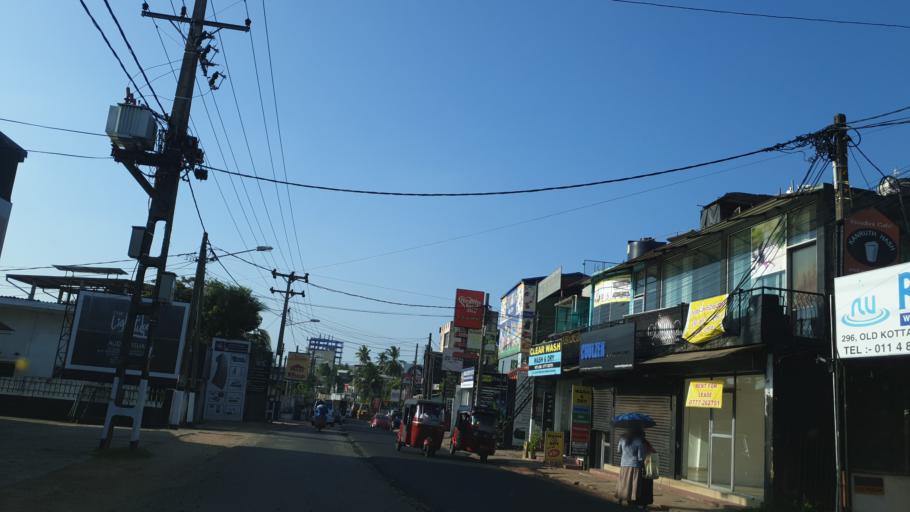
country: LK
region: Western
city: Sri Jayewardenepura Kotte
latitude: 6.8690
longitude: 79.9082
